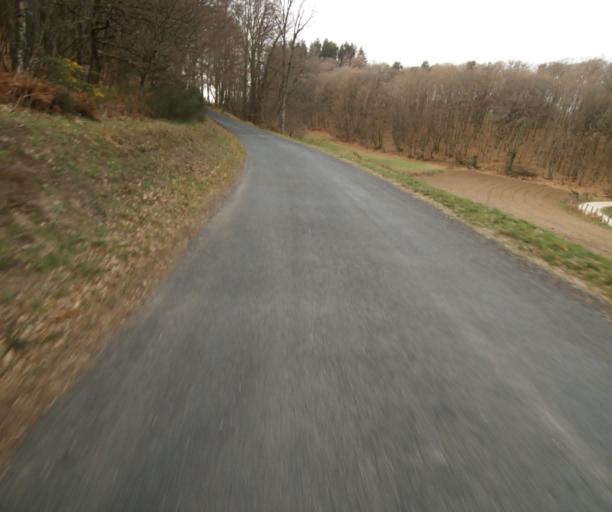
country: FR
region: Limousin
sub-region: Departement de la Correze
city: Treignac
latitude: 45.4492
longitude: 1.8189
